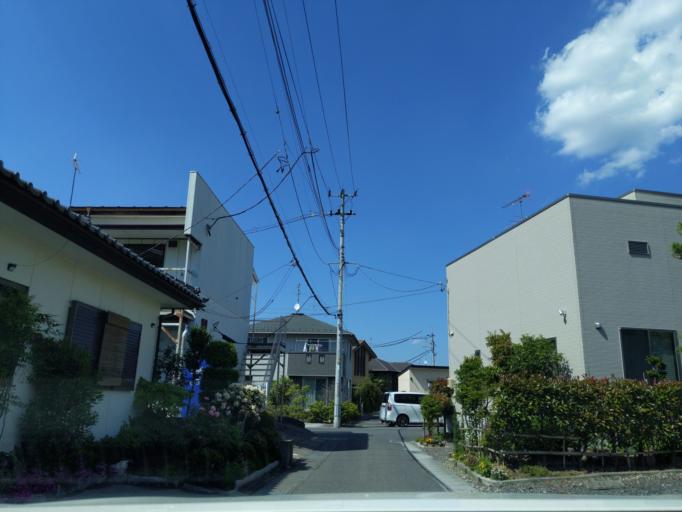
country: JP
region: Fukushima
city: Koriyama
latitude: 37.4102
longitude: 140.3674
